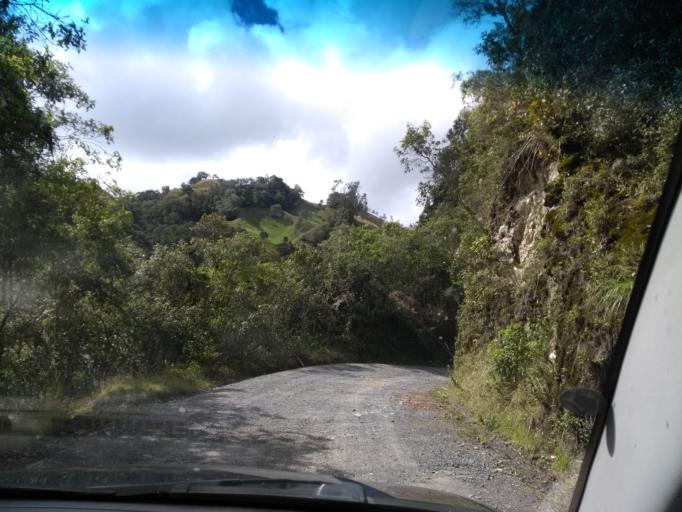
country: CO
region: Caldas
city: Salamina
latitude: 5.3699
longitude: -75.3928
